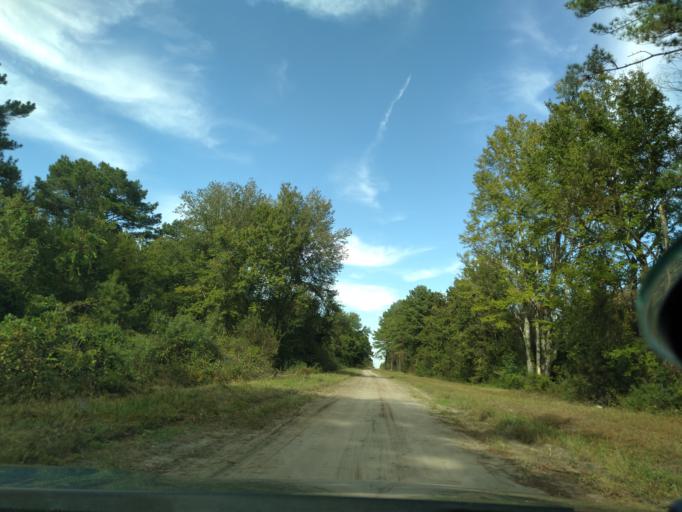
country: US
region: North Carolina
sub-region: Beaufort County
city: Belhaven
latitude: 35.7269
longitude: -76.5765
